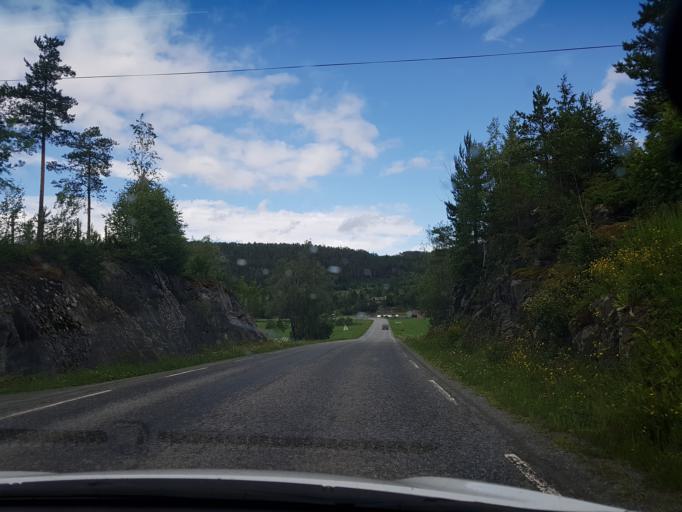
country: NO
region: Nord-Trondelag
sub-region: Stjordal
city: Stjordalshalsen
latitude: 63.6100
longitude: 10.9360
